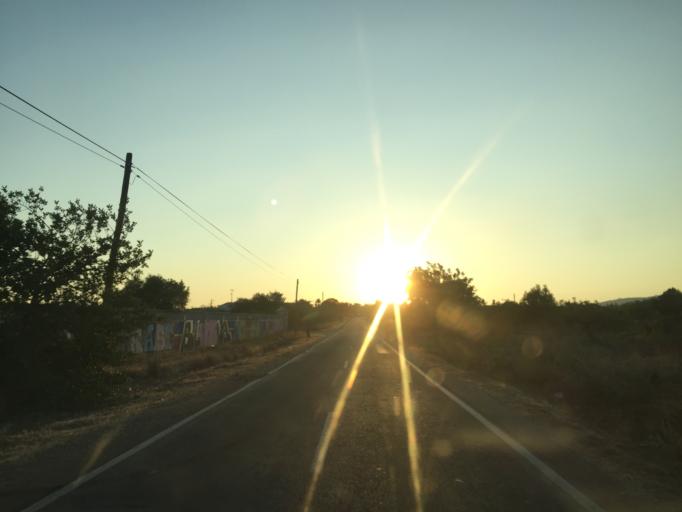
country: PT
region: Faro
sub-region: Faro
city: Santa Barbara de Nexe
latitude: 37.0908
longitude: -7.9333
